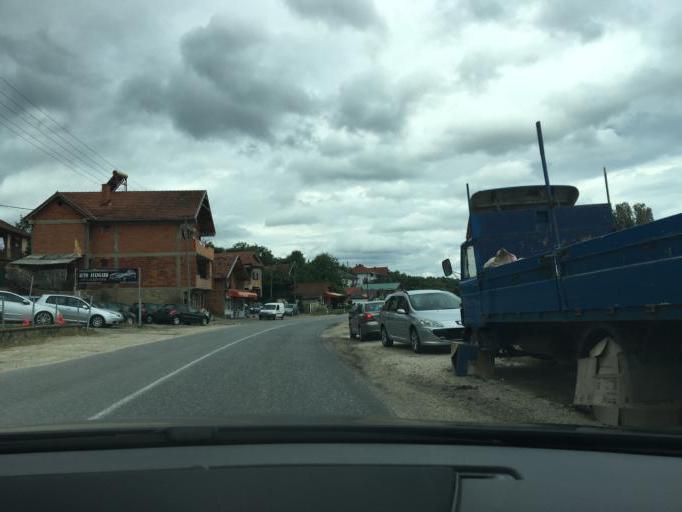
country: MK
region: Kriva Palanka
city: Kriva Palanka
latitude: 42.1891
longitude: 22.3014
